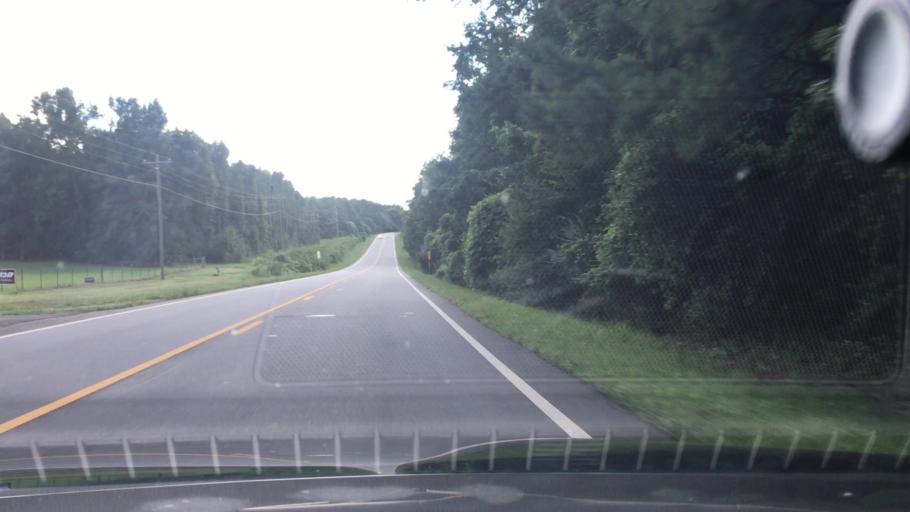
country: US
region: Georgia
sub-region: Butts County
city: Indian Springs
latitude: 33.2888
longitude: -83.8788
